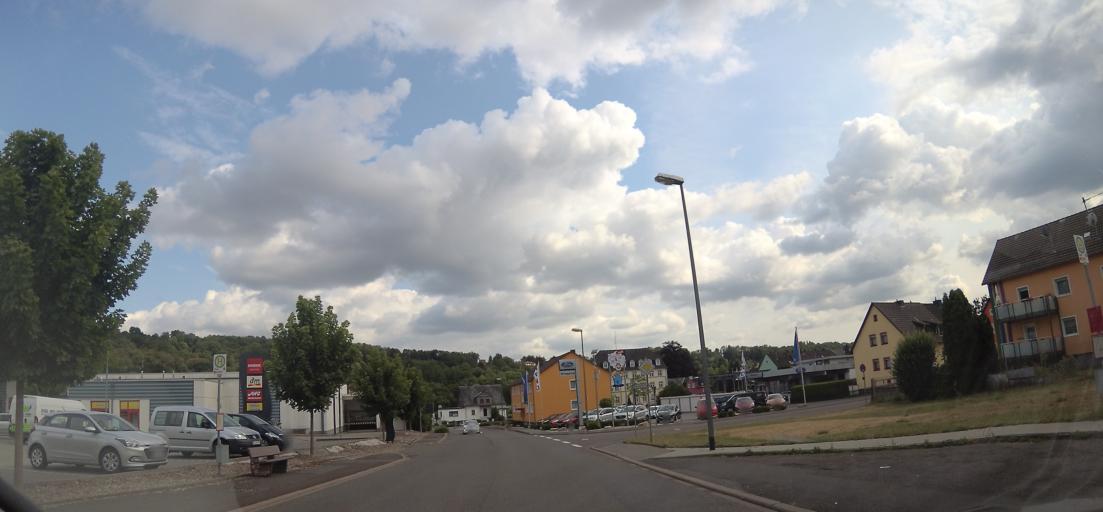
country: DE
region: Rheinland-Pfalz
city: Birkenfeld
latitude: 49.6509
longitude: 7.1723
